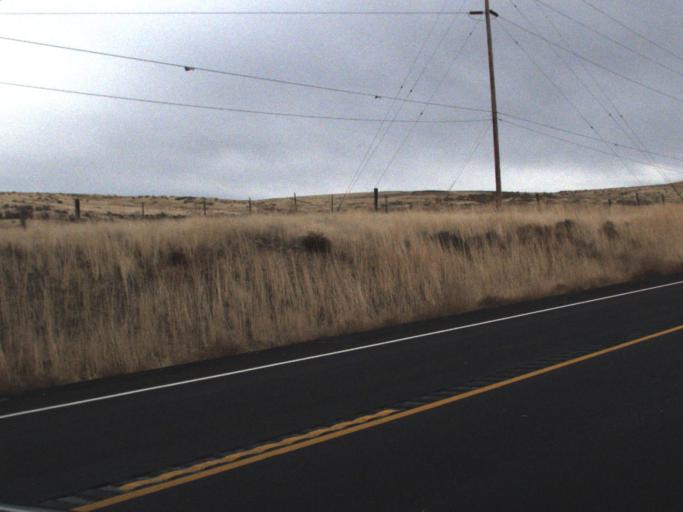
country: US
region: Washington
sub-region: Walla Walla County
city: Burbank
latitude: 46.0693
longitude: -118.7669
